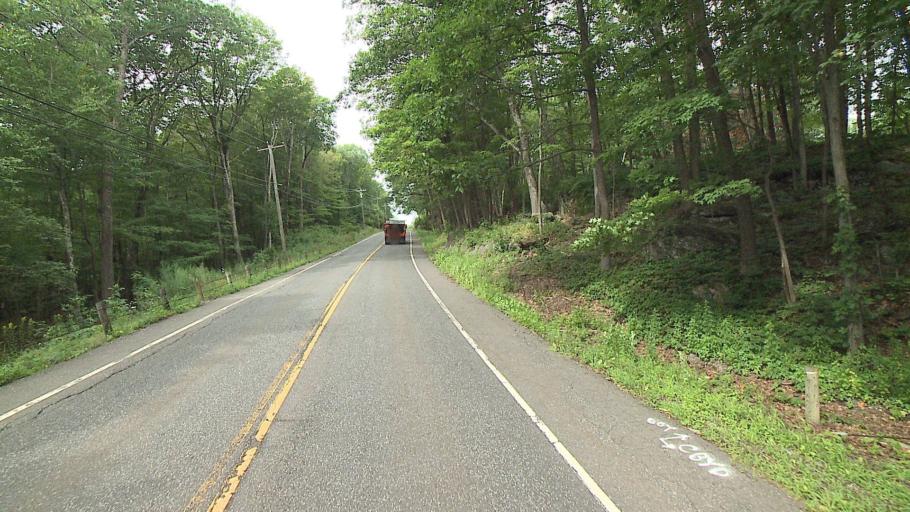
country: US
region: Connecticut
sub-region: Litchfield County
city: New Preston
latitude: 41.7362
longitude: -73.3992
